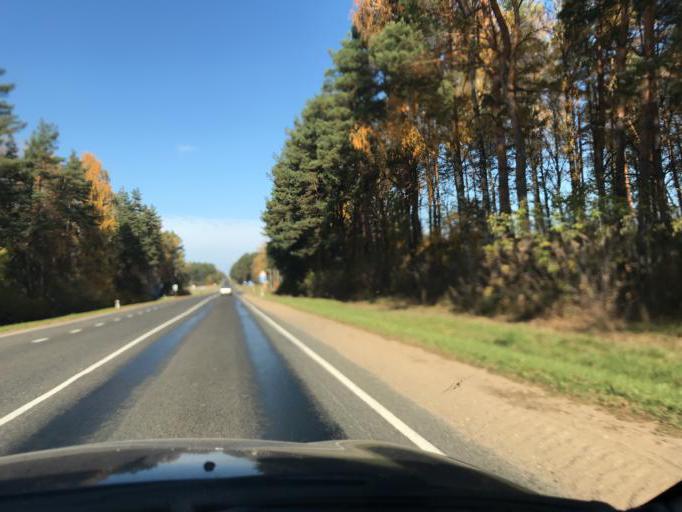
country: BY
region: Grodnenskaya
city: Lida
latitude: 53.9599
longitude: 25.2412
